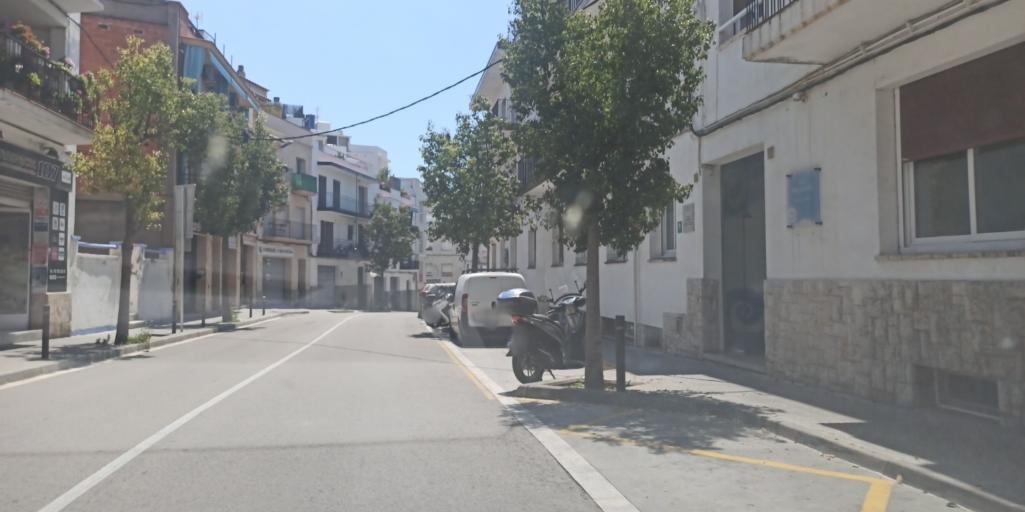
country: ES
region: Catalonia
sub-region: Provincia de Barcelona
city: Sitges
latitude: 41.2399
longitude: 1.8107
